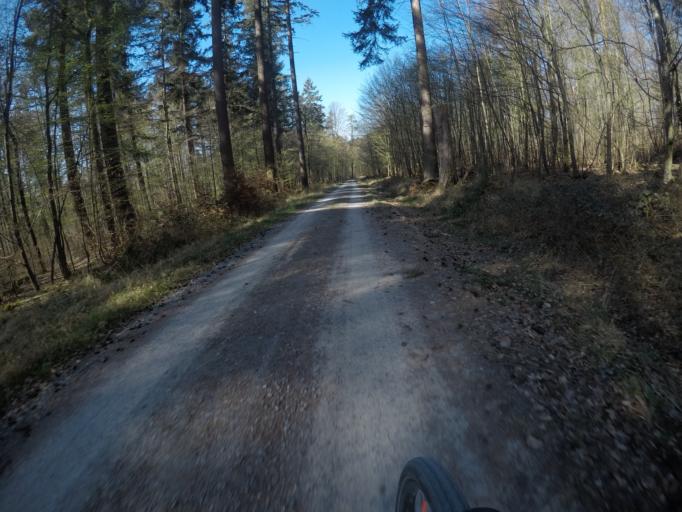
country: DE
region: Baden-Wuerttemberg
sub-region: Regierungsbezirk Stuttgart
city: Weil im Schonbuch
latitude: 48.5927
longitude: 9.0638
